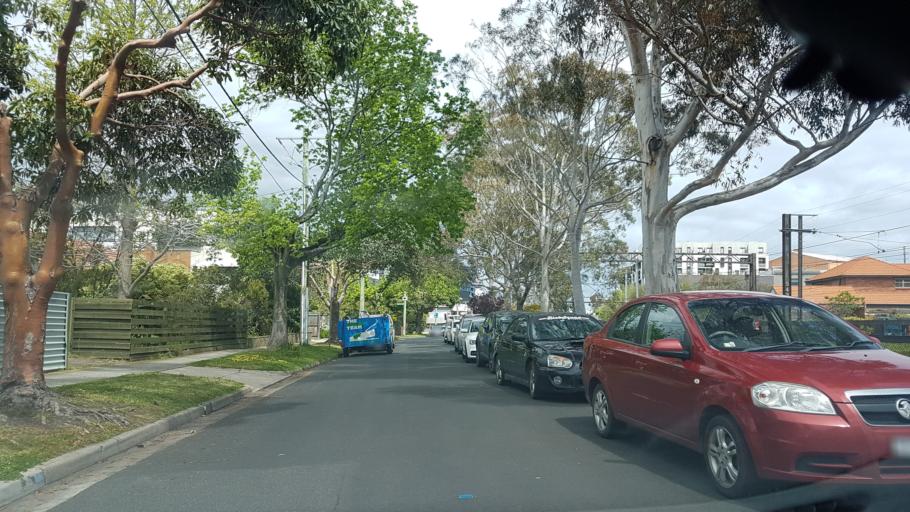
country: AU
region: Victoria
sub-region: Bayside
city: Moorabbin
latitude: -37.9315
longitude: 145.0374
